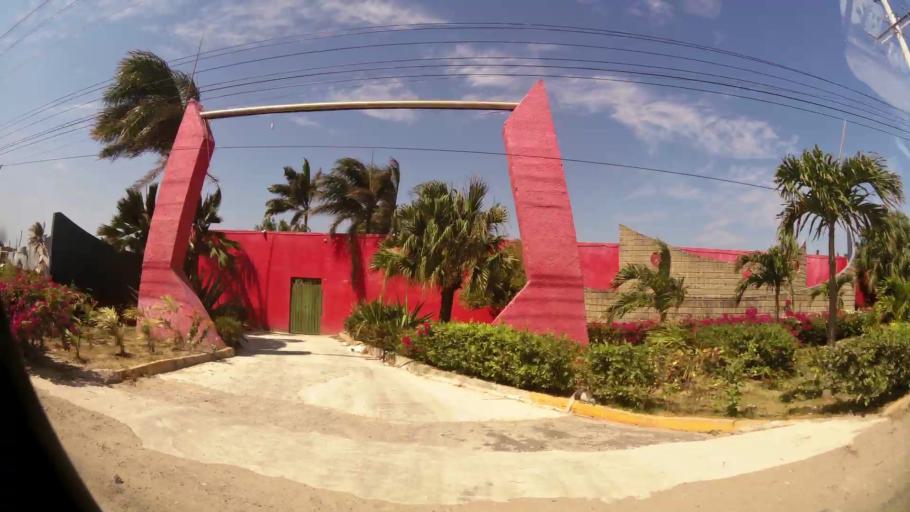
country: CO
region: Atlantico
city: Barranquilla
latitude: 10.9812
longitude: -74.8424
